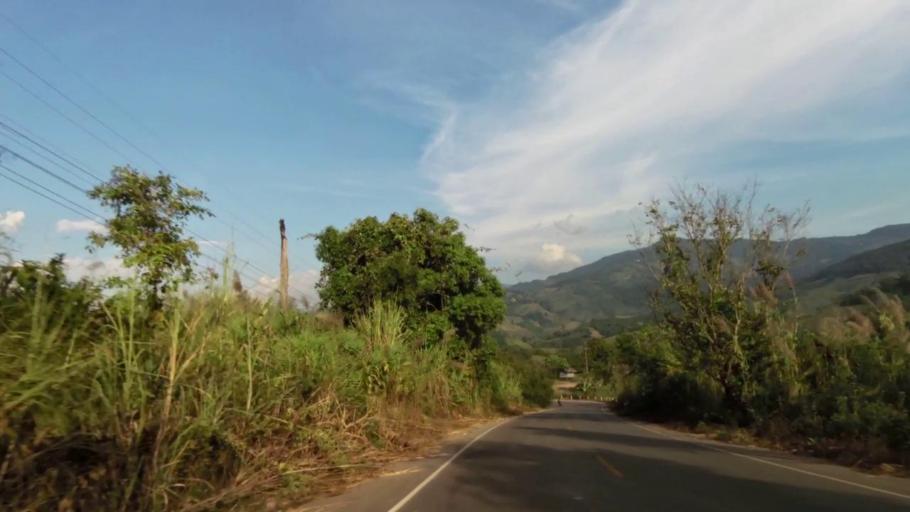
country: TH
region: Chiang Rai
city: Khun Tan
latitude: 19.8589
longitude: 100.3915
